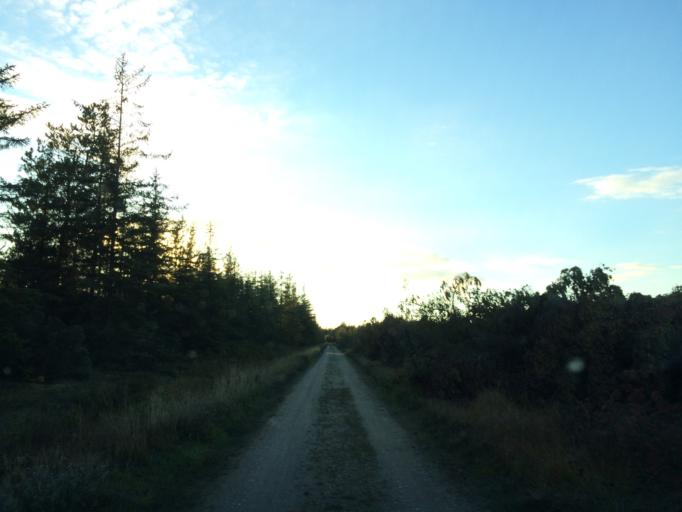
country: DK
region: Central Jutland
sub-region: Holstebro Kommune
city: Ulfborg
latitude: 56.3063
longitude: 8.1483
